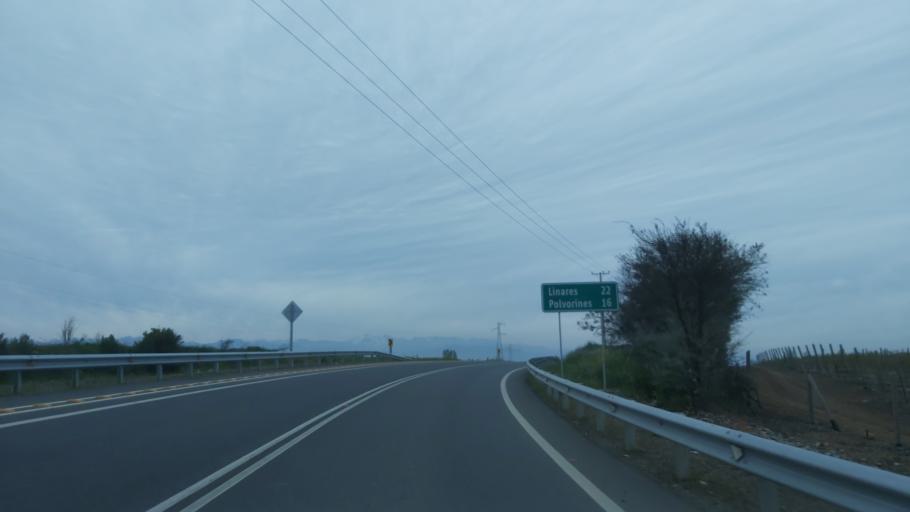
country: CL
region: Maule
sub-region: Provincia de Linares
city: Colbun
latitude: -35.6998
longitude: -71.4873
